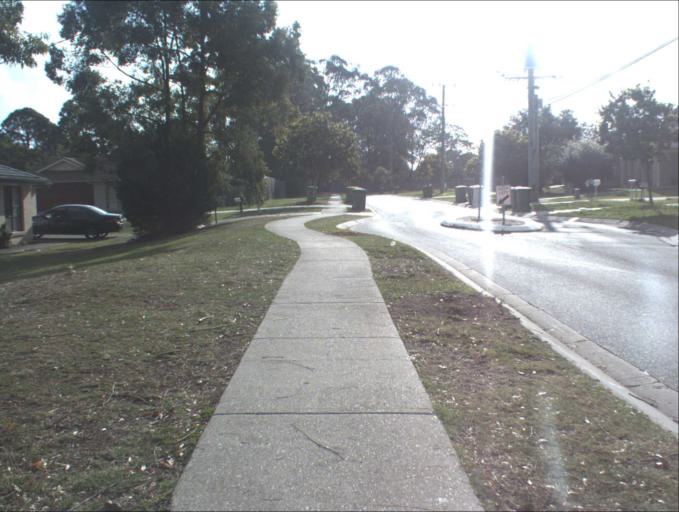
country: AU
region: Queensland
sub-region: Logan
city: Waterford West
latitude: -27.6790
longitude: 153.1272
